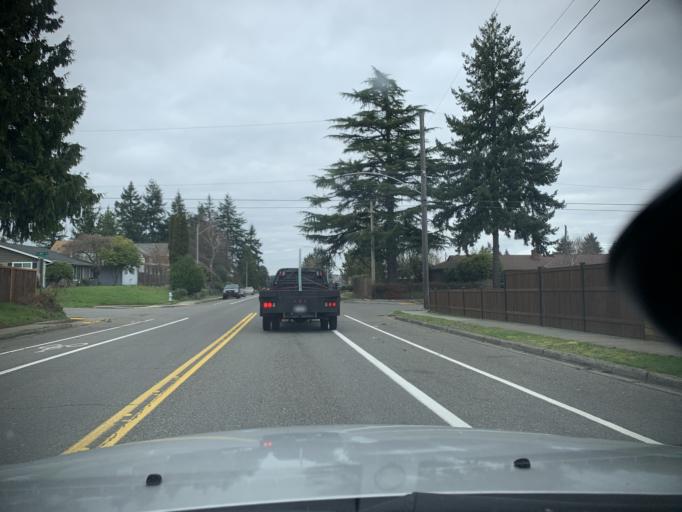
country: US
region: Washington
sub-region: Pierce County
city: Fircrest
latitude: 47.2941
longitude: -122.5210
